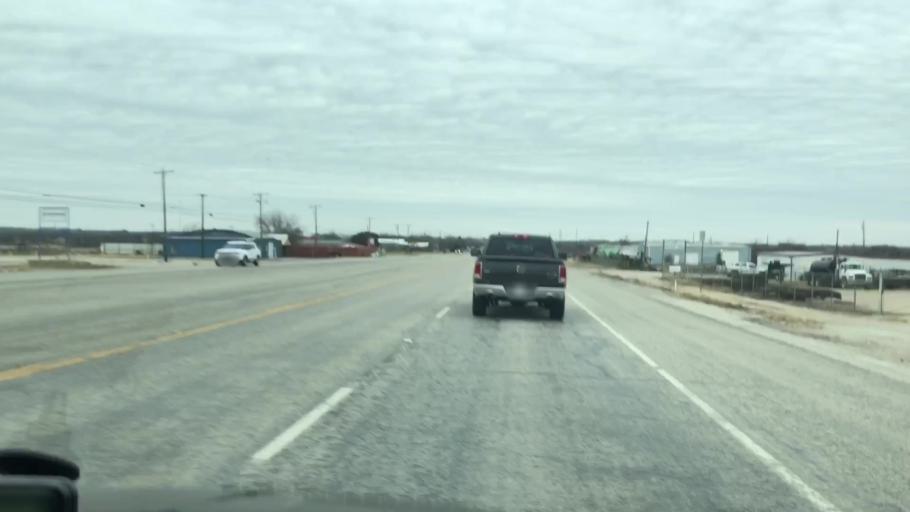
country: US
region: Texas
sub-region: Jack County
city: Jacksboro
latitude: 33.2013
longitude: -98.1498
